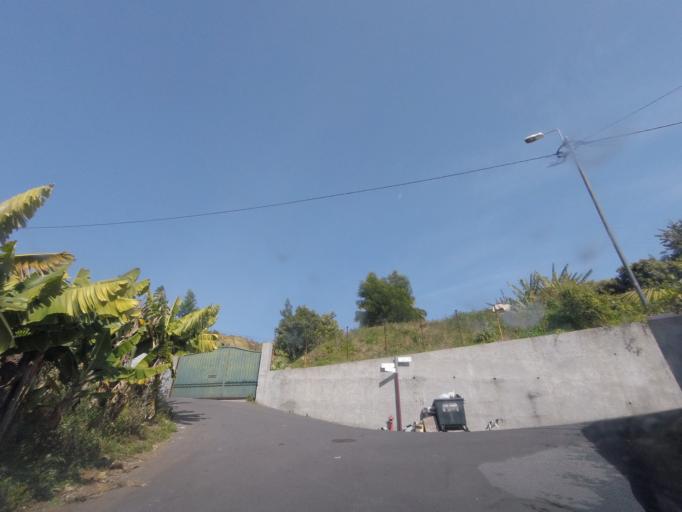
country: PT
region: Madeira
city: Camara de Lobos
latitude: 32.6502
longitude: -16.9521
